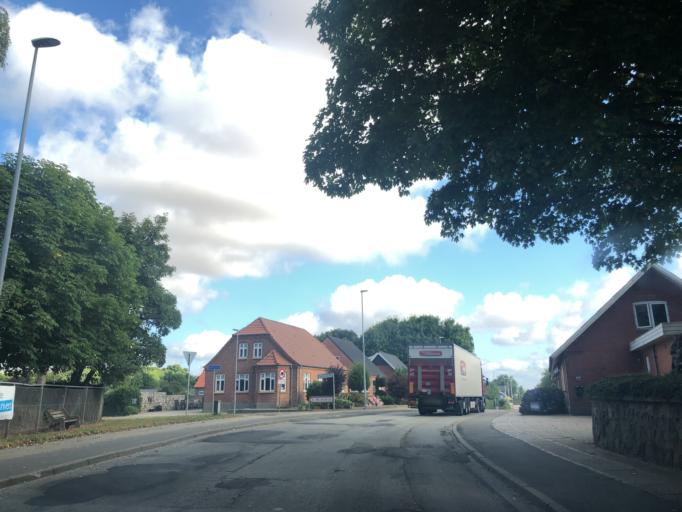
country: DK
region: Central Jutland
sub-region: Skive Kommune
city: Skive
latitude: 56.6500
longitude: 8.9328
